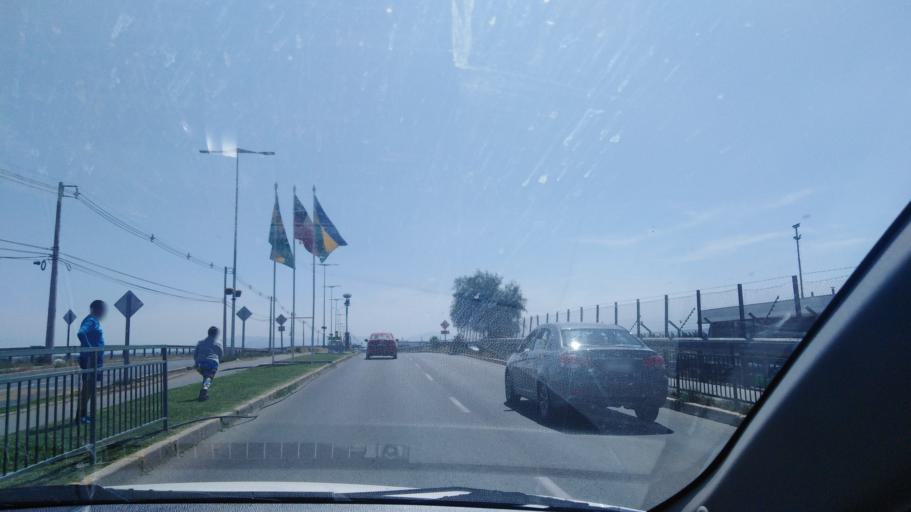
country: CL
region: Santiago Metropolitan
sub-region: Provincia de Santiago
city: Lo Prado
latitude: -33.3482
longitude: -70.7288
